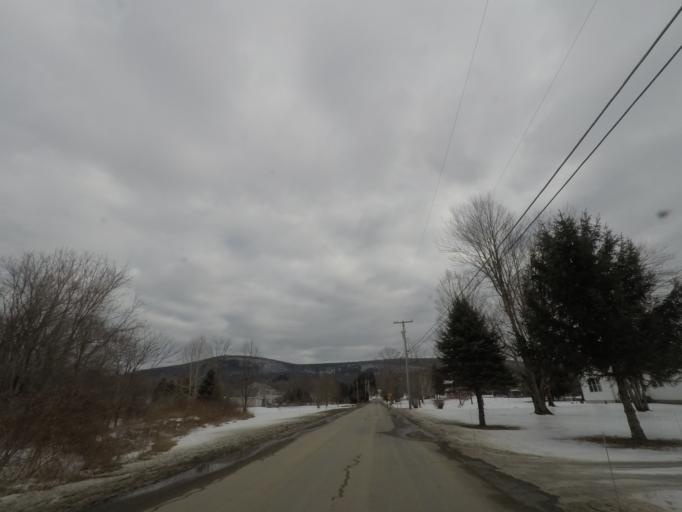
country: US
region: New York
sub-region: Rensselaer County
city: Poestenkill
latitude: 42.7367
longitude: -73.5661
